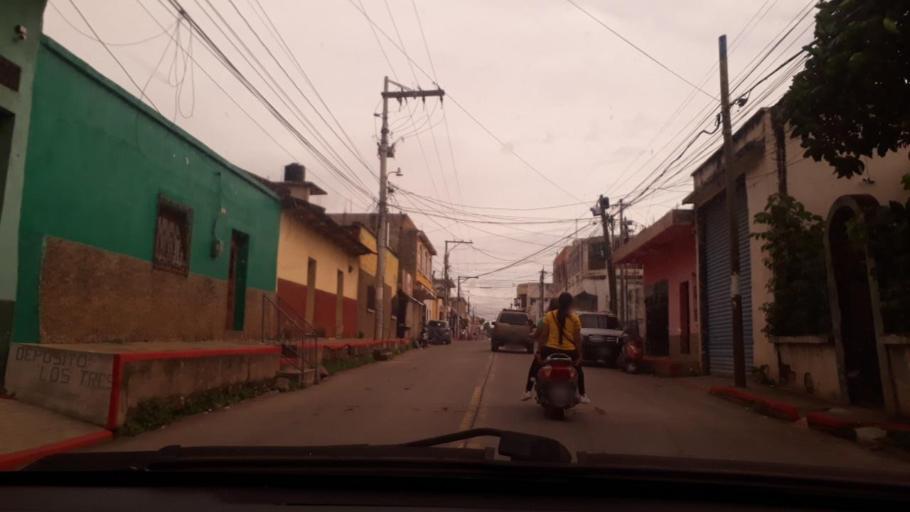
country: GT
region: Jutiapa
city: Jutiapa
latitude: 14.2965
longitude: -89.8957
